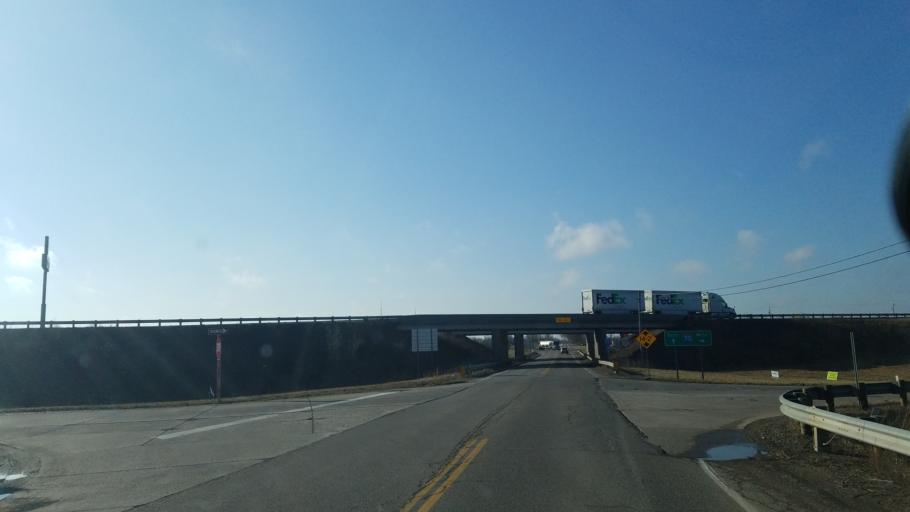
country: US
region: Ohio
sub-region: Guernsey County
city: Byesville
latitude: 40.0338
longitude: -81.4470
